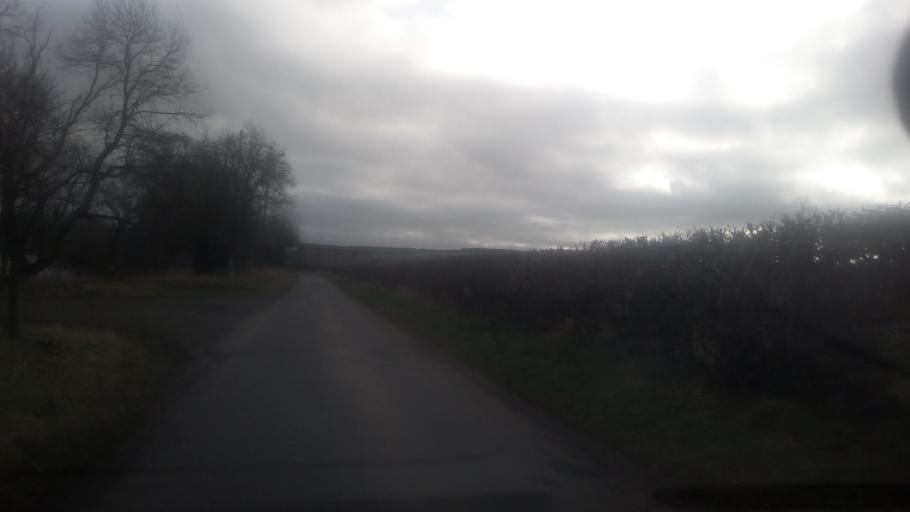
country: GB
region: Scotland
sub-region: The Scottish Borders
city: Kelso
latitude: 55.5454
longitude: -2.4742
